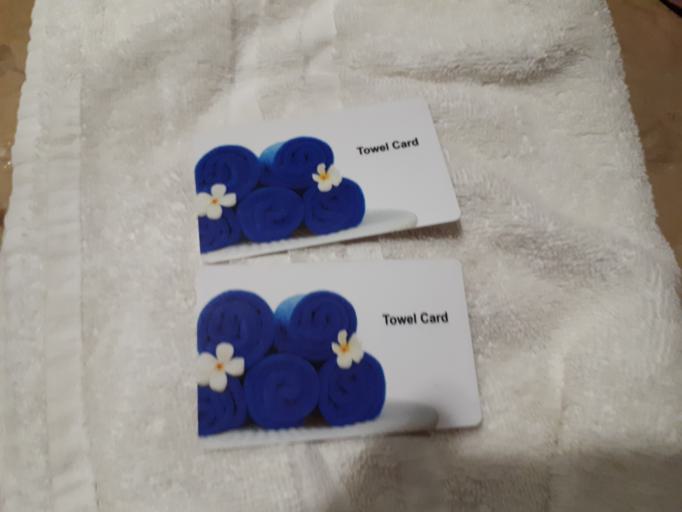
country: TR
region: Antalya
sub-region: Alanya
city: Payallar
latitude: 36.5858
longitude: 31.8722
